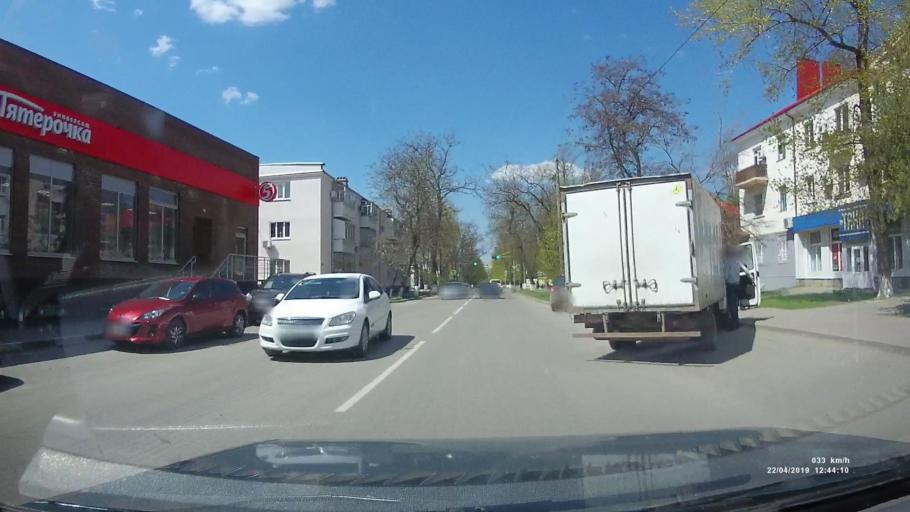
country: RU
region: Rostov
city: Azov
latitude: 47.1033
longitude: 39.4189
